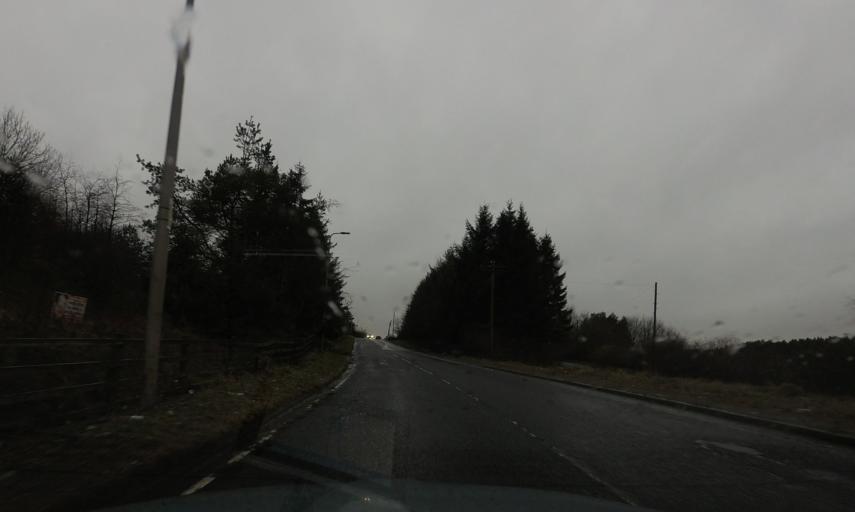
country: GB
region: Scotland
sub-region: North Lanarkshire
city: Shotts
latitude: 55.8565
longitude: -3.7873
